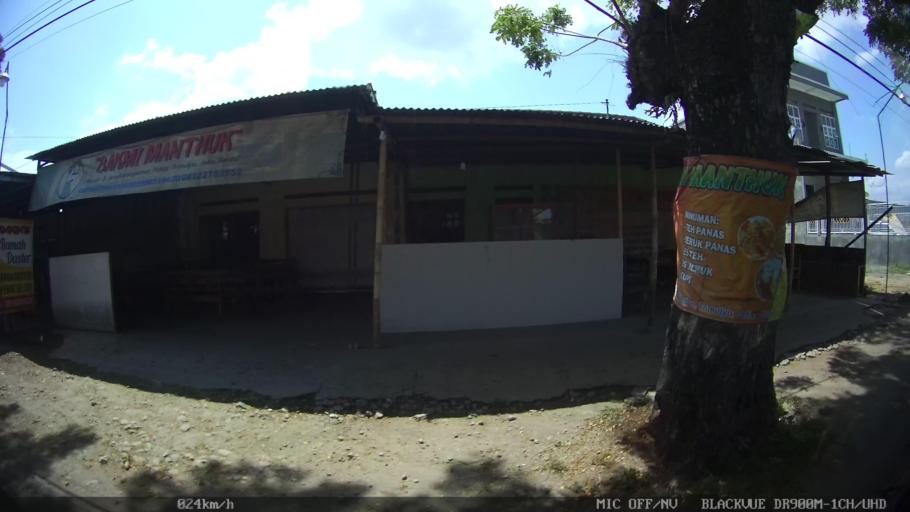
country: ID
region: Daerah Istimewa Yogyakarta
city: Sewon
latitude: -7.8982
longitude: 110.3804
